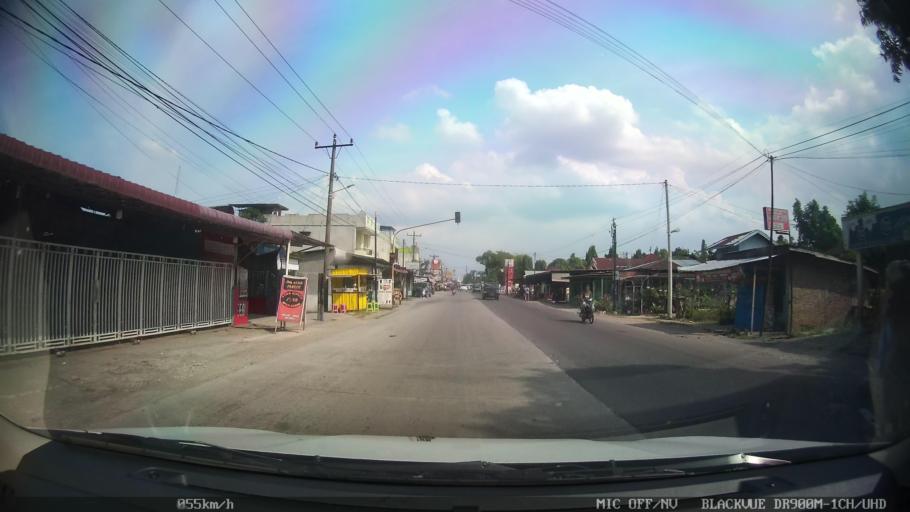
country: ID
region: North Sumatra
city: Binjai
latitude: 3.6308
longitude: 98.4916
